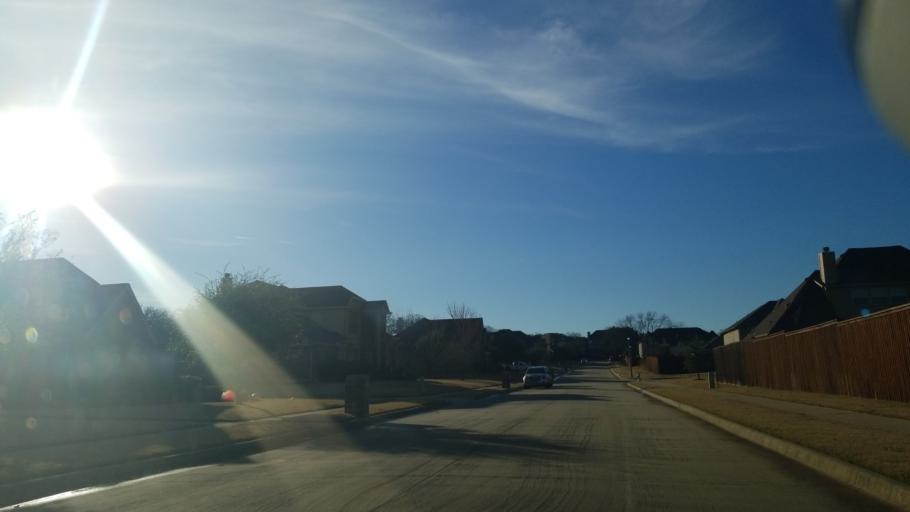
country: US
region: Texas
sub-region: Denton County
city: Corinth
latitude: 33.1510
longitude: -97.0735
